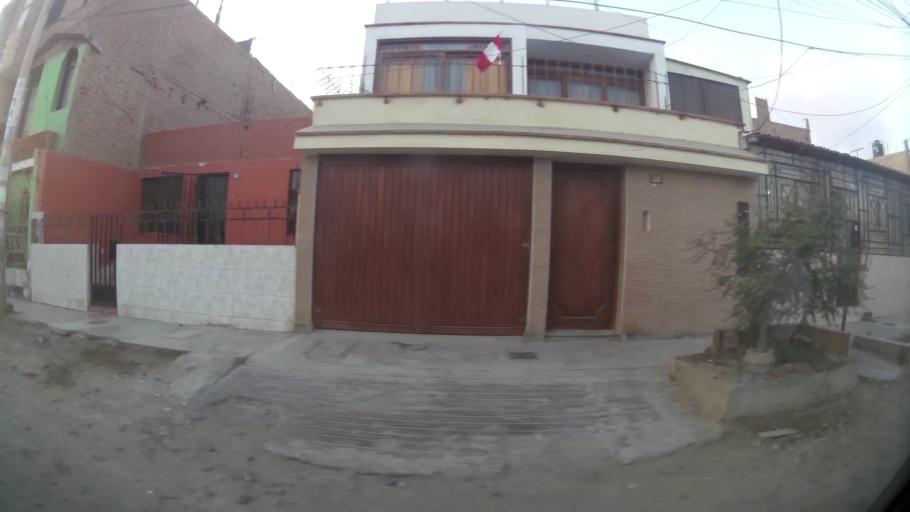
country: PE
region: Lima
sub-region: Huaura
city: Huacho
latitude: -11.1163
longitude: -77.6091
